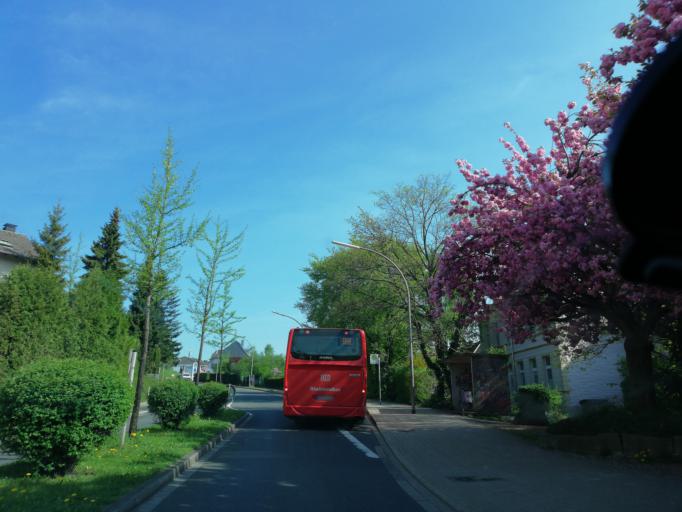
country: DE
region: North Rhine-Westphalia
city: Wetter (Ruhr)
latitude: 51.3720
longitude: 7.3699
